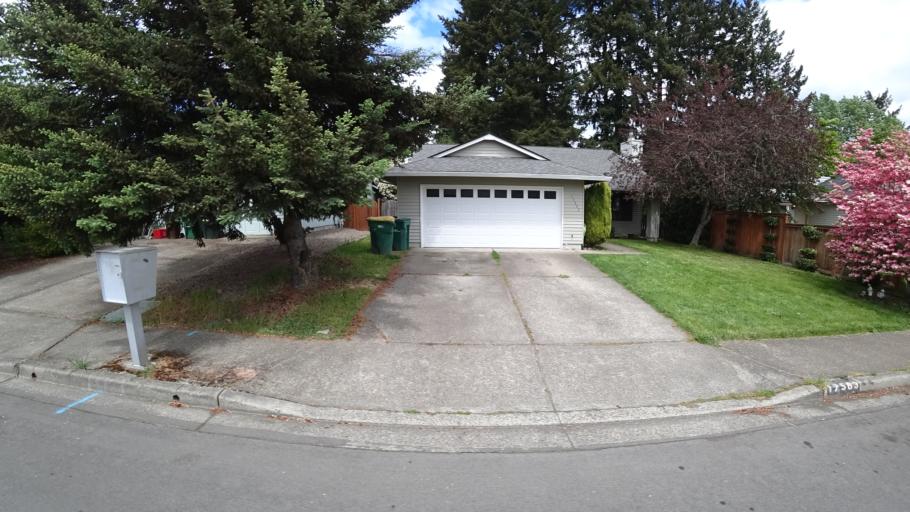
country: US
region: Oregon
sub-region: Washington County
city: Aloha
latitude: 45.4694
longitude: -122.8586
